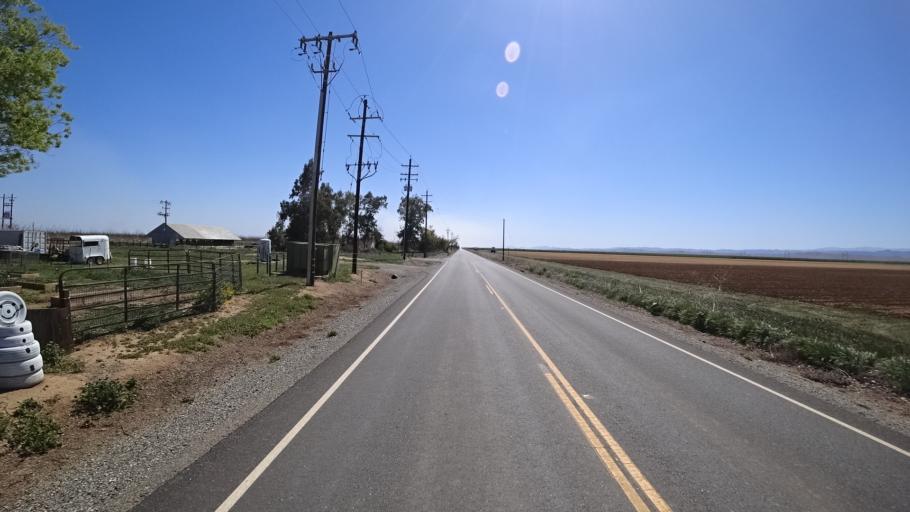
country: US
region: California
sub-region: Glenn County
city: Willows
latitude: 39.5101
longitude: -122.2491
